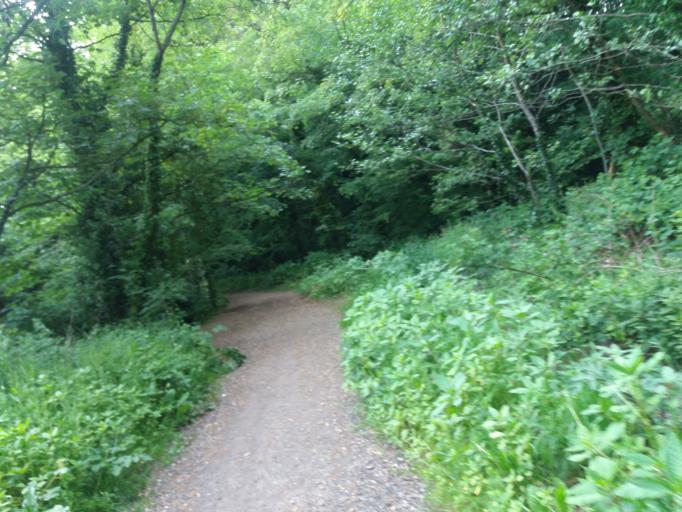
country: GB
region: England
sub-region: Lancashire
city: Coppull
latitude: 53.6494
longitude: -2.6574
